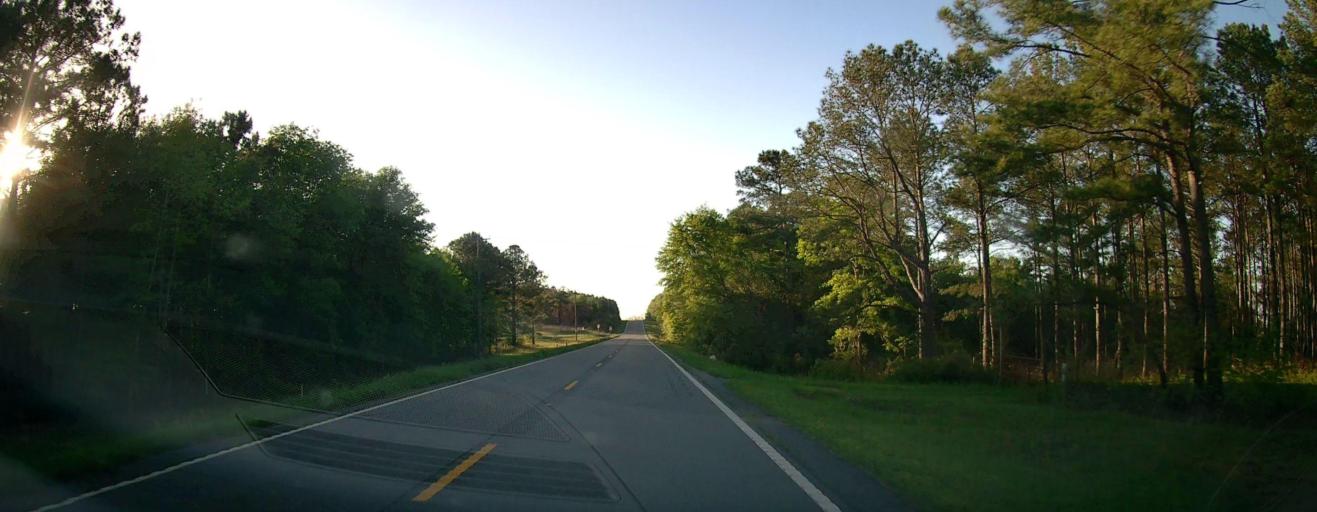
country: US
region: Georgia
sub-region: Schley County
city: Ellaville
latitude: 32.3362
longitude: -84.3514
